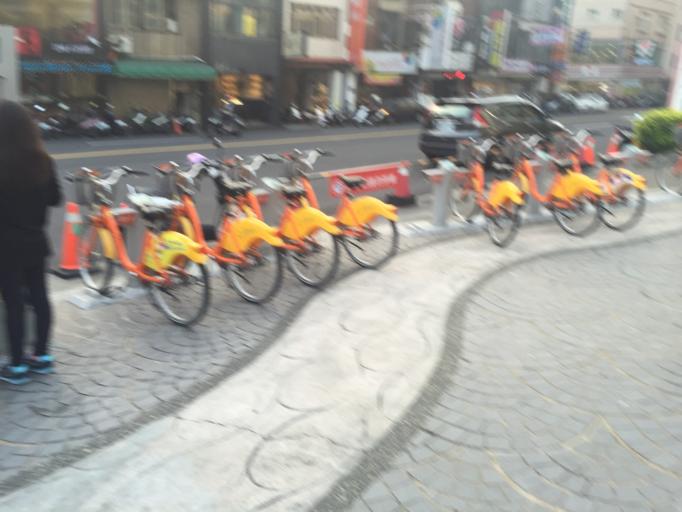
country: TW
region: Taiwan
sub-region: Hsinchu
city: Hsinchu
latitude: 24.8093
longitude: 120.9743
